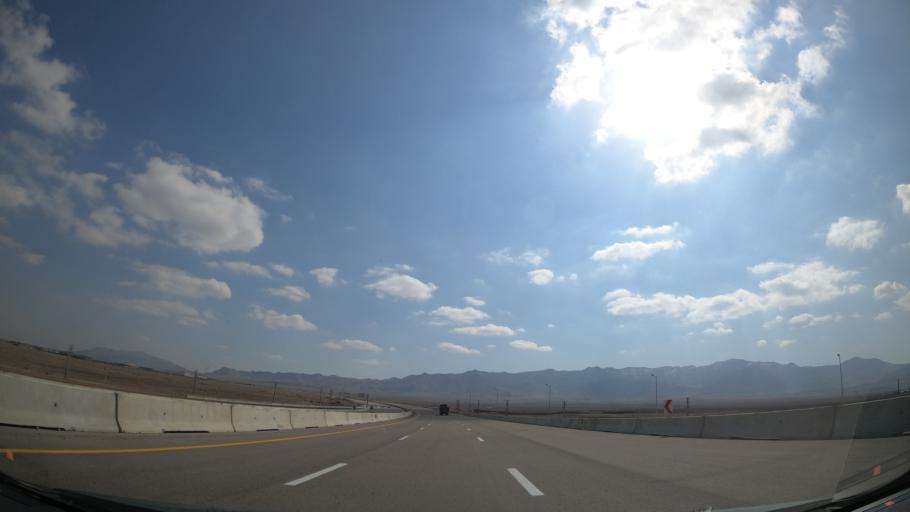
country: IR
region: Alborz
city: Eshtehard
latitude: 35.7294
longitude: 50.5615
